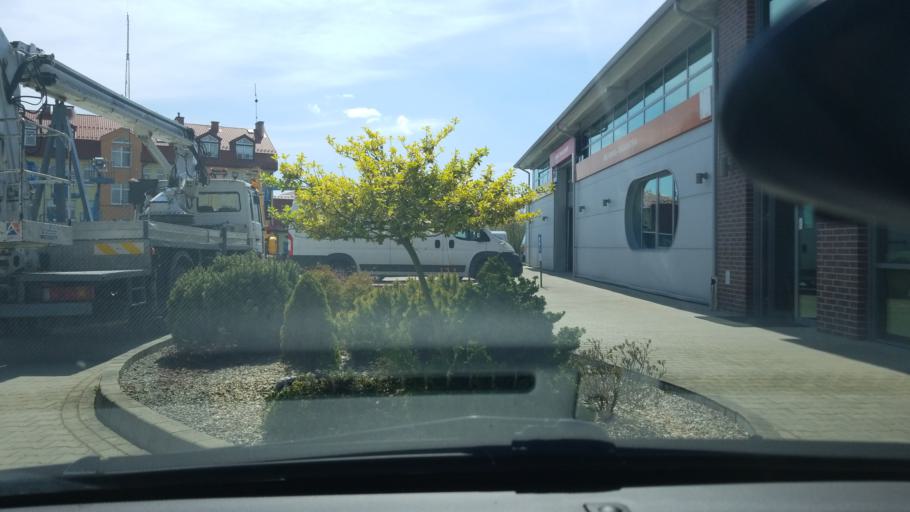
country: PL
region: Subcarpathian Voivodeship
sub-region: Powiat jasielski
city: Jaslo
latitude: 49.7393
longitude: 21.4844
